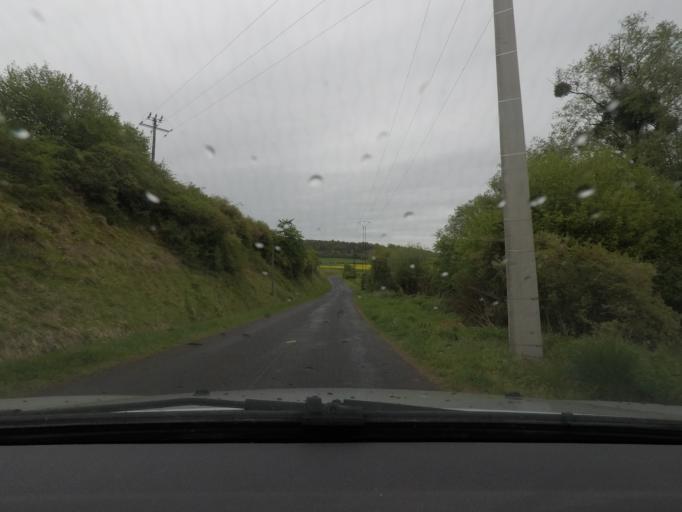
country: BE
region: Wallonia
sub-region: Province du Luxembourg
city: Rouvroy
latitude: 49.4972
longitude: 5.4340
